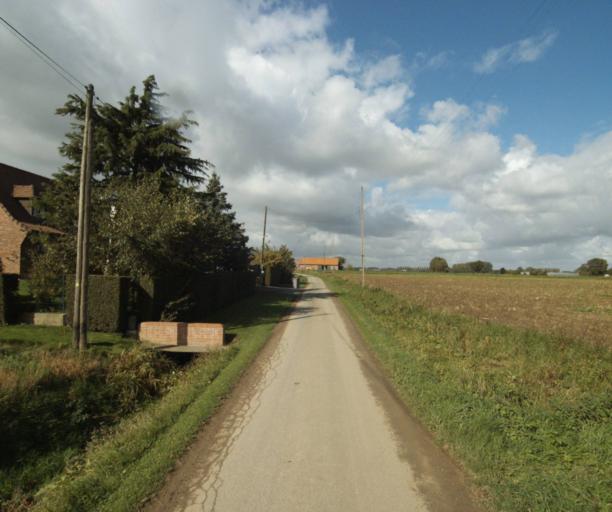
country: FR
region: Nord-Pas-de-Calais
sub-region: Departement du Nord
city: Perenchies
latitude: 50.6916
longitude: 2.9608
